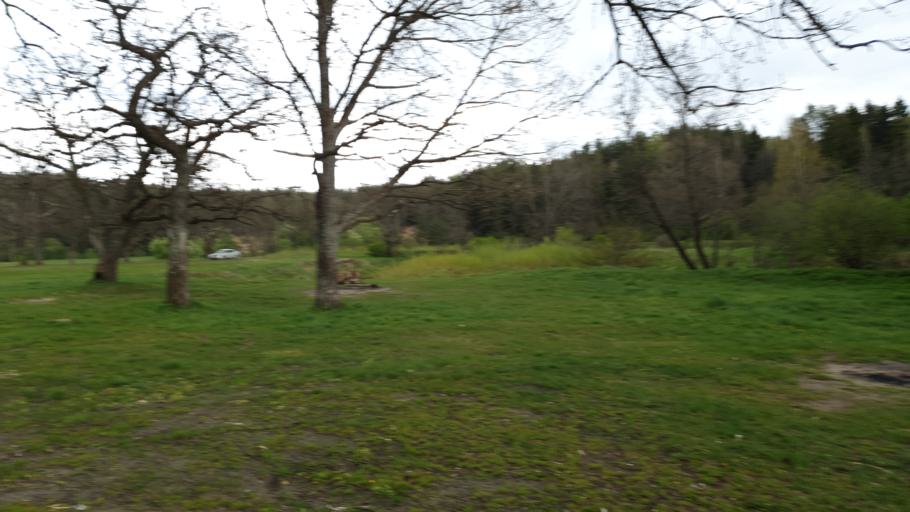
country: BY
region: Minsk
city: Rakaw
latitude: 53.9803
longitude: 26.9726
